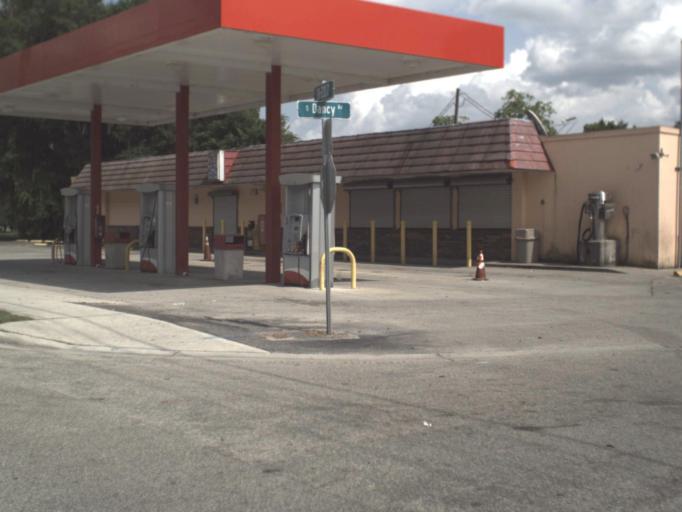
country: US
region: Florida
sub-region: Putnam County
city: East Palatka
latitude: 29.7143
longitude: -81.5124
